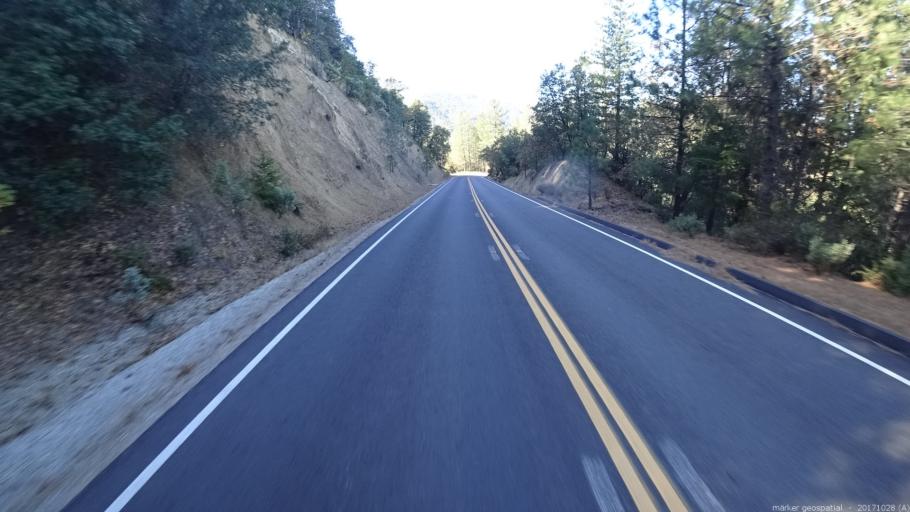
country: US
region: California
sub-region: Shasta County
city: Shasta
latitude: 40.6093
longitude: -122.5630
